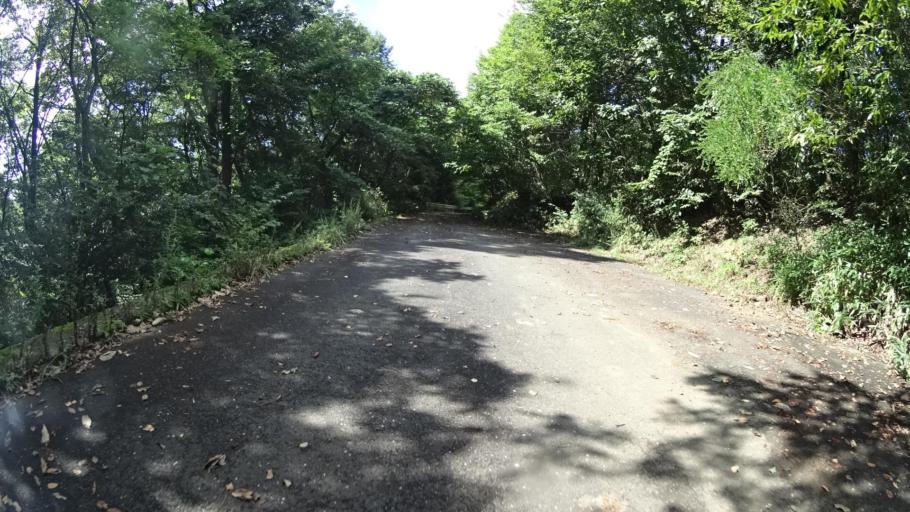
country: JP
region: Yamanashi
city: Uenohara
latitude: 35.7463
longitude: 139.0476
